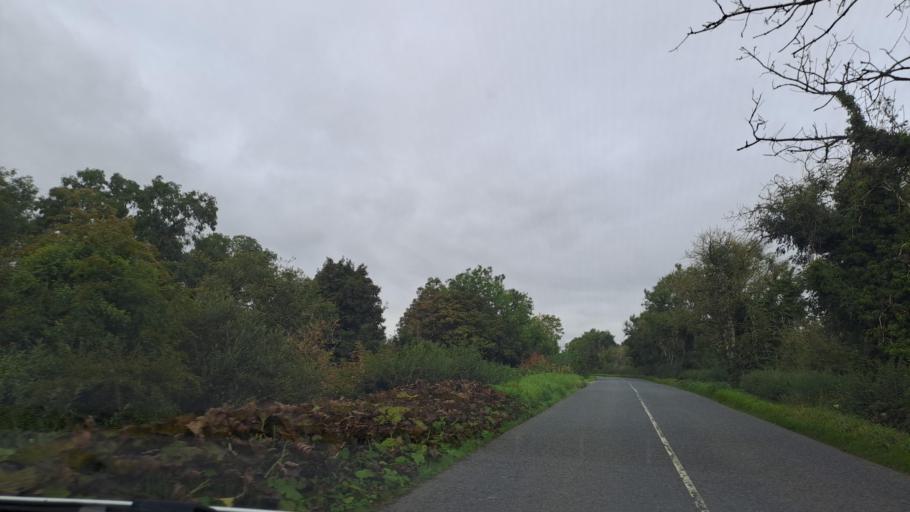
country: IE
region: Ulster
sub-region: An Cabhan
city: Kingscourt
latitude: 53.8842
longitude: -6.7374
